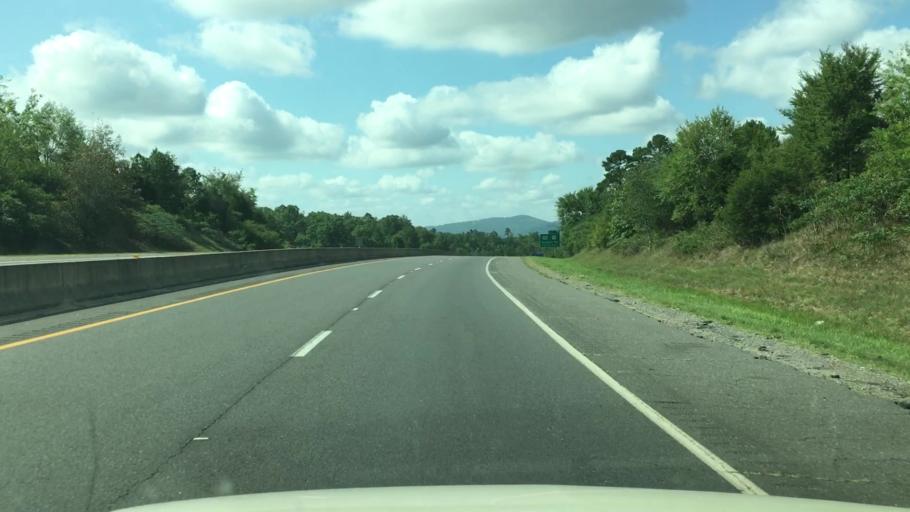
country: US
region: Arkansas
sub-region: Garland County
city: Piney
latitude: 34.4894
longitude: -93.1118
